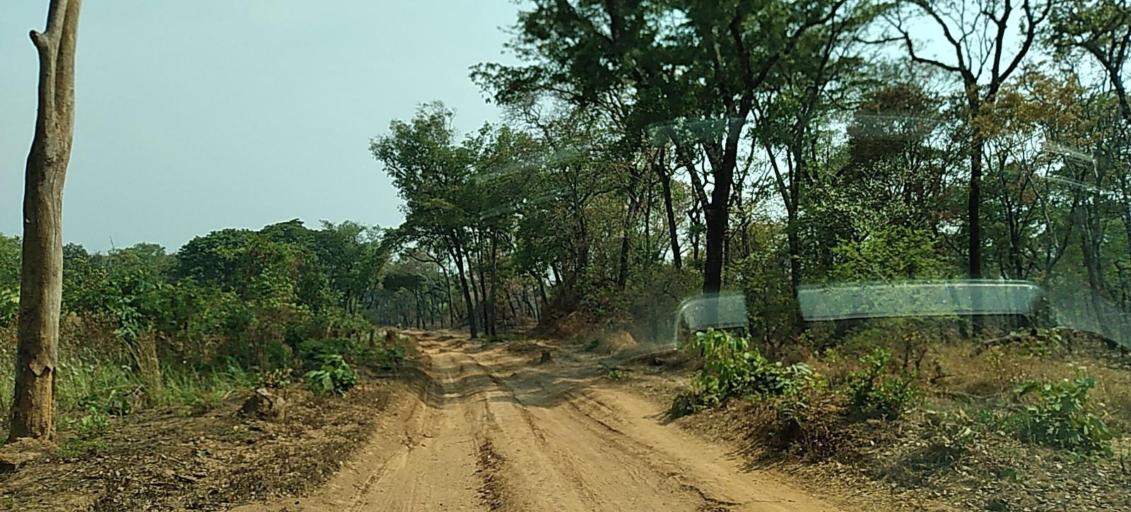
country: ZM
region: North-Western
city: Kansanshi
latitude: -12.0640
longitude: 26.8893
